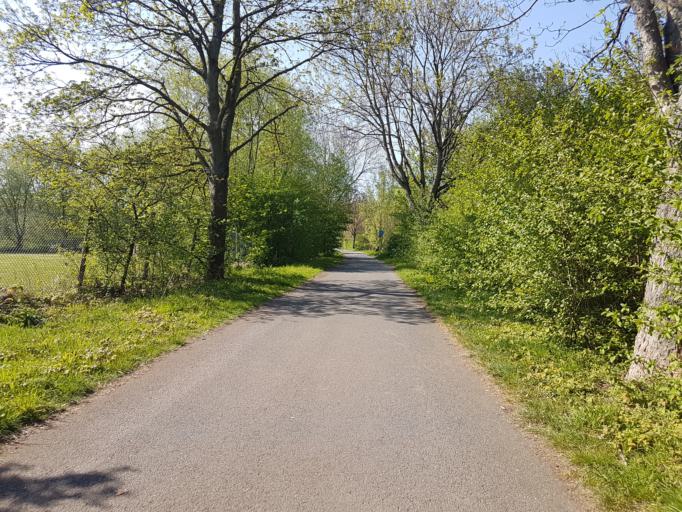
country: DE
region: North Rhine-Westphalia
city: Witten
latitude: 51.4304
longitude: 7.2879
